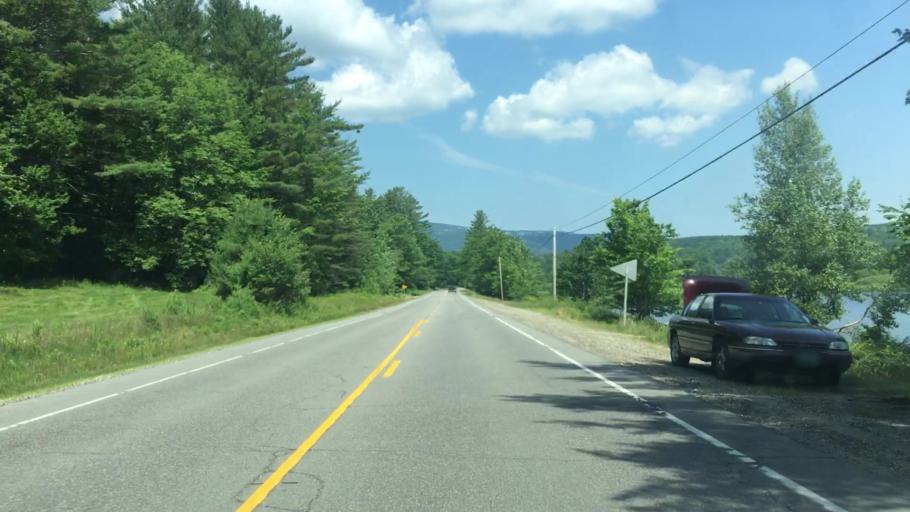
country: US
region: New Hampshire
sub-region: Sullivan County
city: Grantham
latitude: 43.4441
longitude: -72.1584
